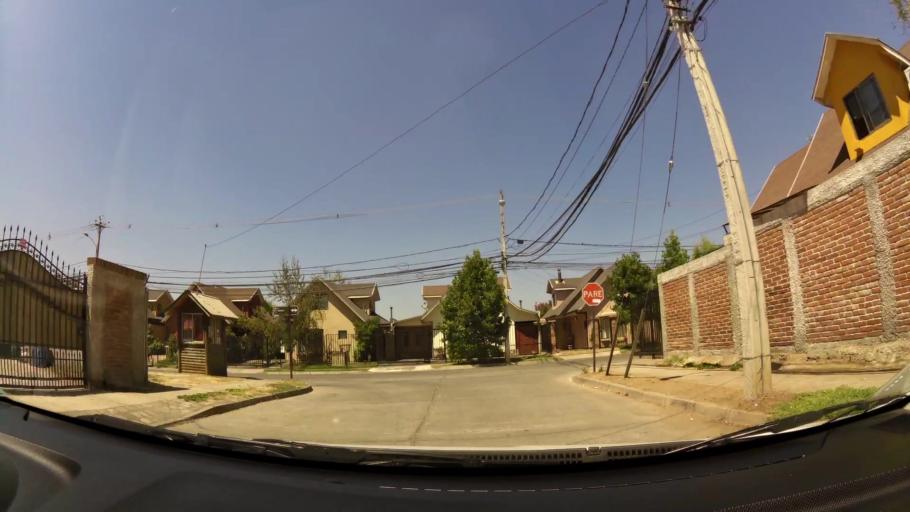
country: CL
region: Maule
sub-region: Provincia de Talca
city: Talca
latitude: -35.4260
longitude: -71.6193
